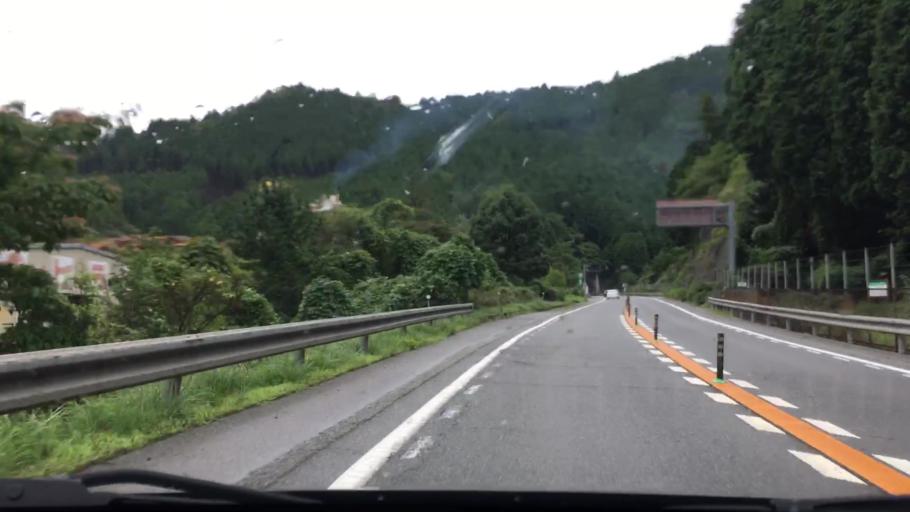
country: JP
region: Hyogo
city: Nishiwaki
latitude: 35.1478
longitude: 134.7881
